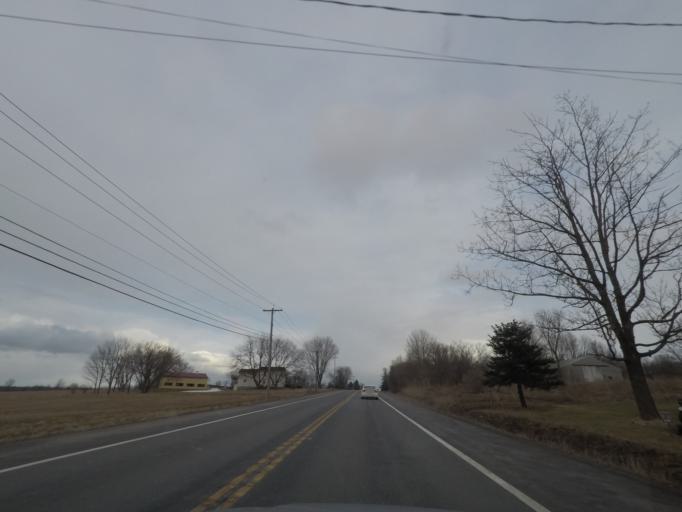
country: US
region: New York
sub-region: Oneida County
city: Vernon
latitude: 43.0734
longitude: -75.5091
